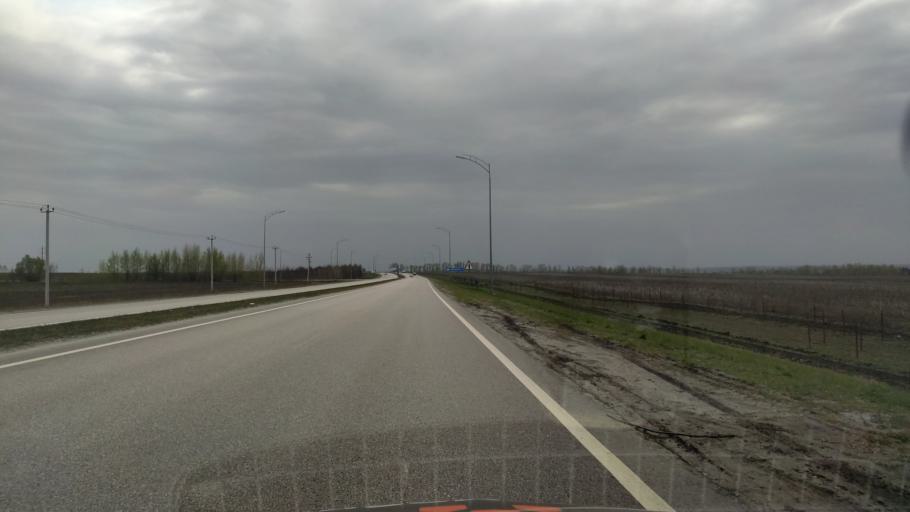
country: RU
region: Belgorod
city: Staryy Oskol
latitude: 51.3835
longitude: 37.8575
